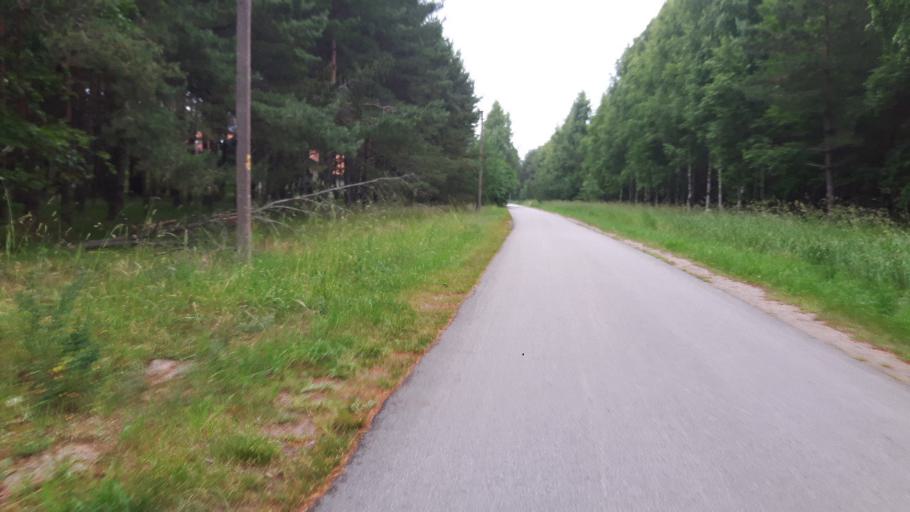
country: LT
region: Klaipedos apskritis
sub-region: Palanga
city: Sventoji
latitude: 55.9938
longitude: 21.0756
